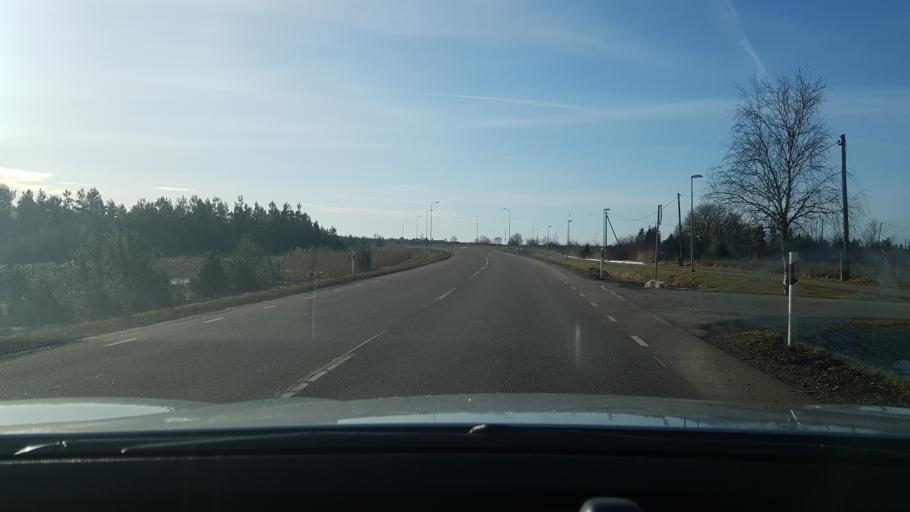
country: EE
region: Saare
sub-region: Kuressaare linn
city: Kuressaare
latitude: 58.2386
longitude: 22.5009
